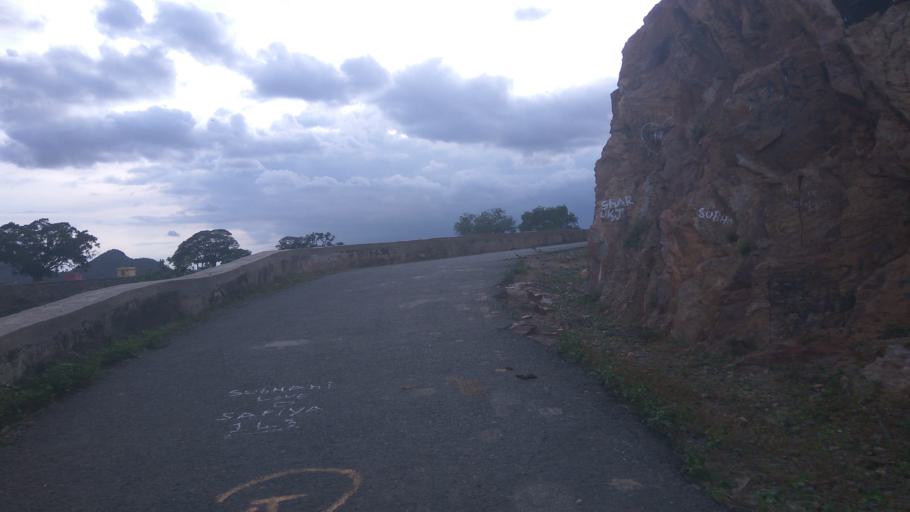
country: IN
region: Andhra Pradesh
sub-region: Prakasam
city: Cumbum
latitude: 15.5769
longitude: 79.0836
